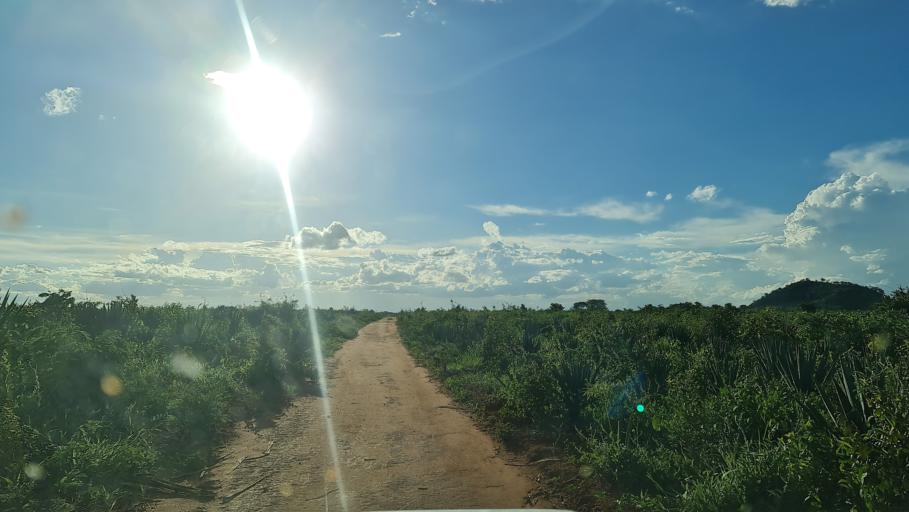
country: MZ
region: Nampula
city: Ilha de Mocambique
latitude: -14.9528
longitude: 40.1841
